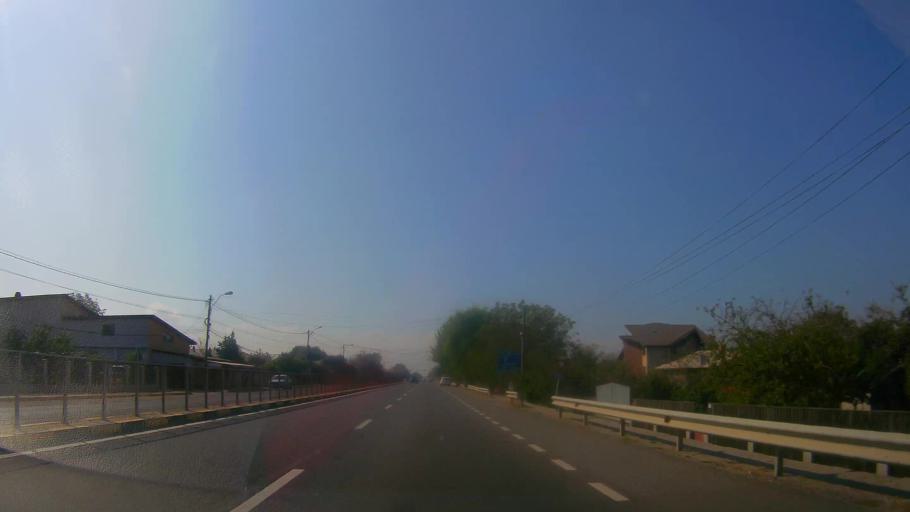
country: RO
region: Giurgiu
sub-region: Comuna Fratesti
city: Remus
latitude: 43.9394
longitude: 25.9782
